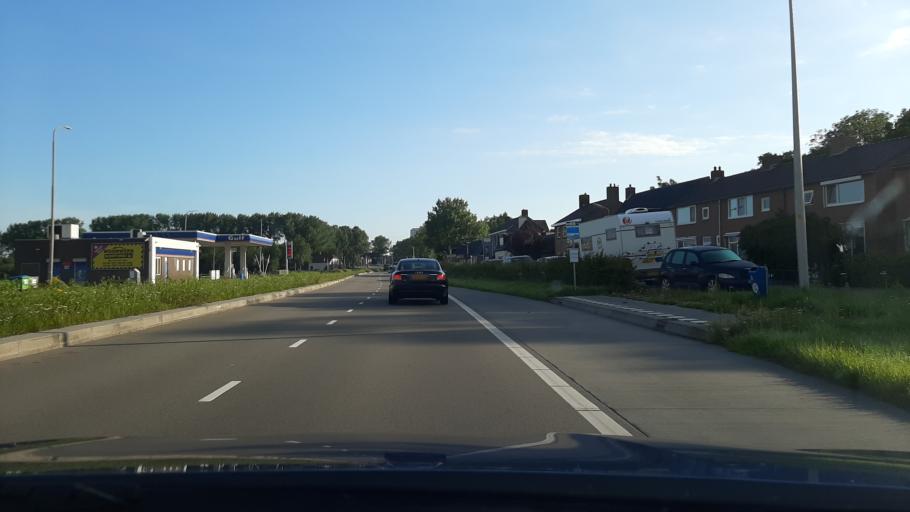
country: NL
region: Friesland
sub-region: Gemeente Leeuwarden
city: Goutum
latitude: 53.1768
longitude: 5.7951
